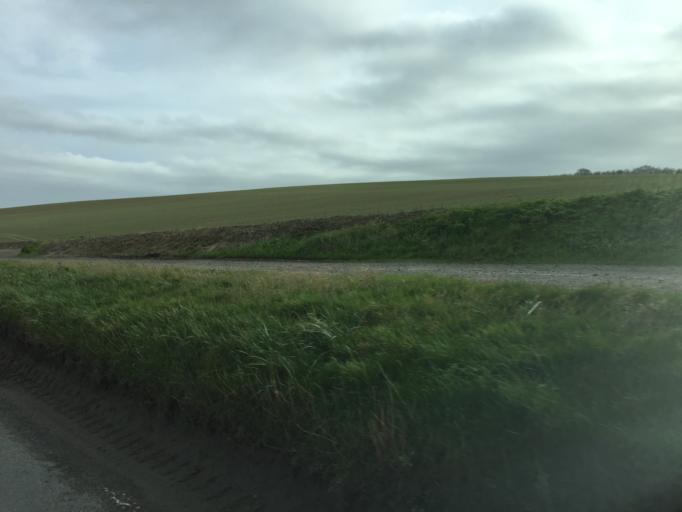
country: GB
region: England
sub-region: Oxfordshire
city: Blewbury
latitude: 51.5664
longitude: -1.2200
